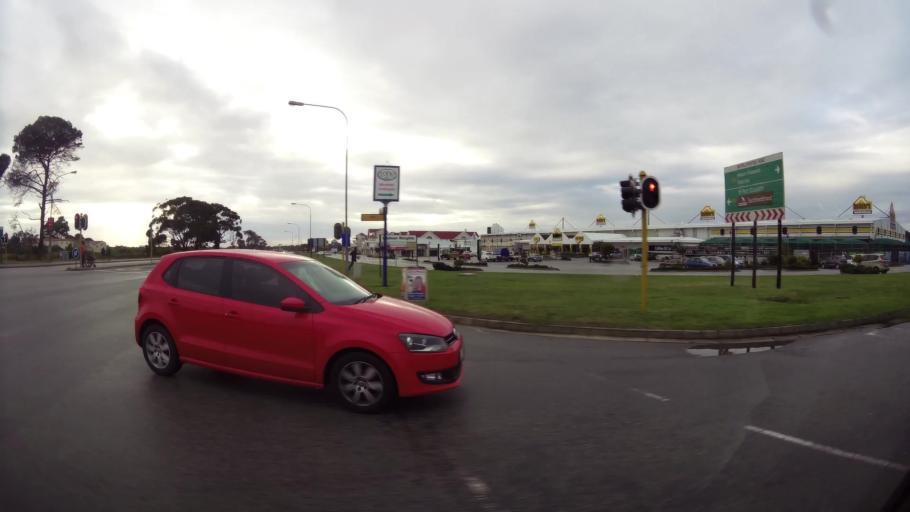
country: ZA
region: Eastern Cape
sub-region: Nelson Mandela Bay Metropolitan Municipality
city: Port Elizabeth
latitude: -33.9916
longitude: 25.5520
